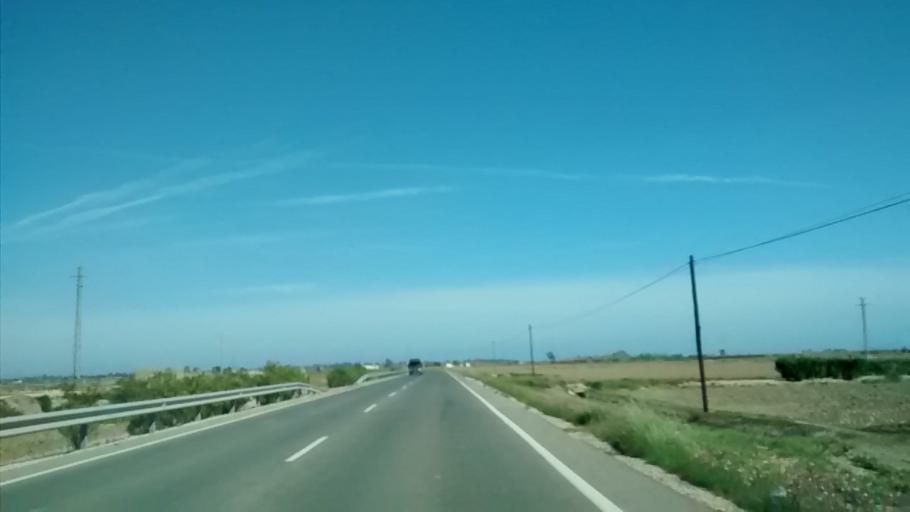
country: ES
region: Catalonia
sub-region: Provincia de Tarragona
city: Deltebre
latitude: 40.7045
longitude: 0.7892
